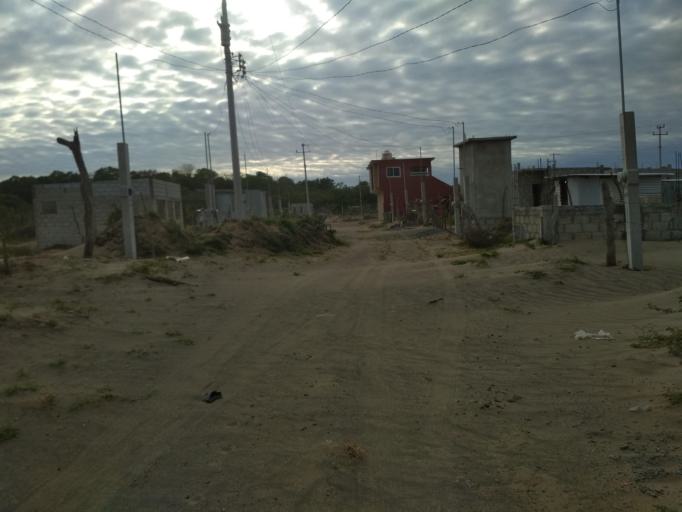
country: MX
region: Veracruz
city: Anton Lizardo
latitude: 19.0438
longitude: -95.9919
